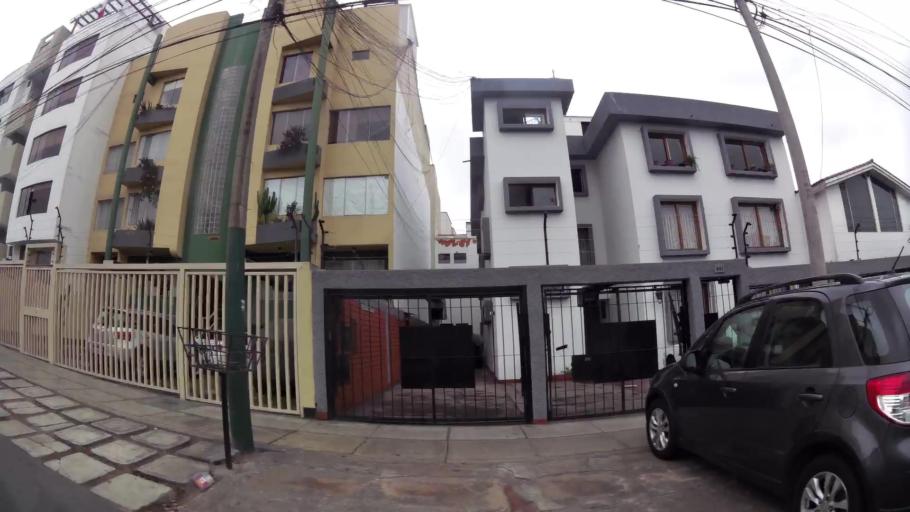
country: PE
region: Lima
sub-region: Lima
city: Surco
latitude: -12.1146
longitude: -76.9950
